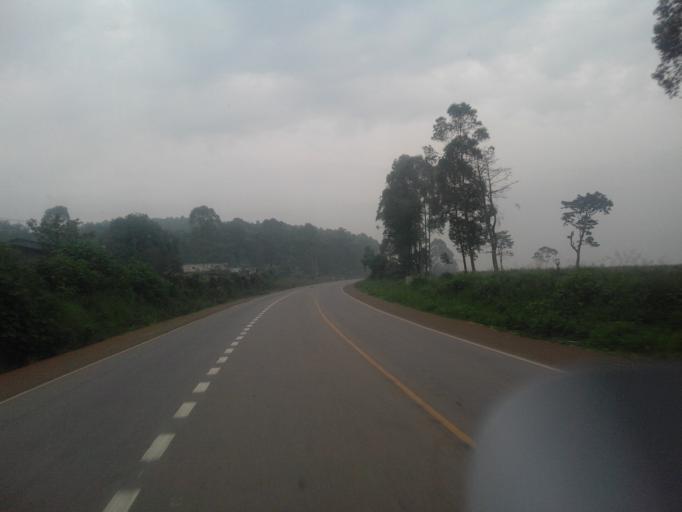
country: UG
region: Central Region
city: Lugazi
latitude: 0.3723
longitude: 32.8958
